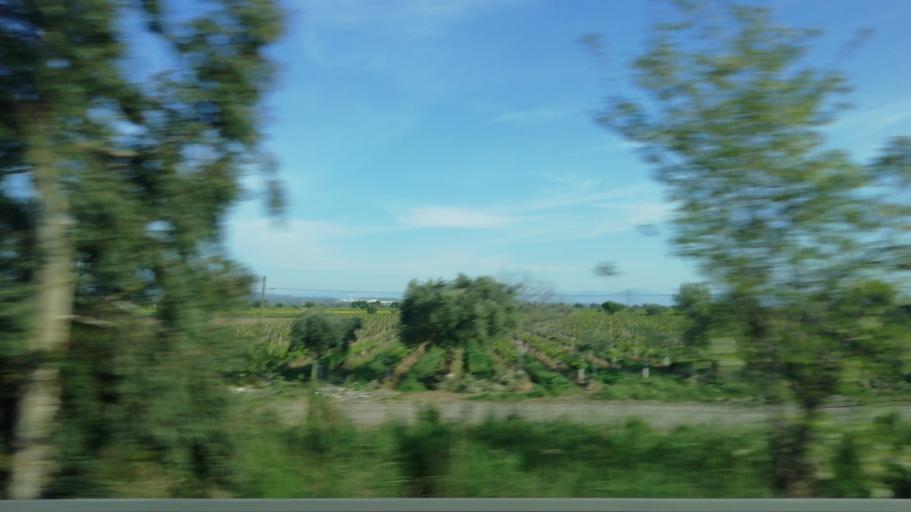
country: TR
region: Manisa
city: Saruhanli
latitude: 38.7229
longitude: 27.5662
